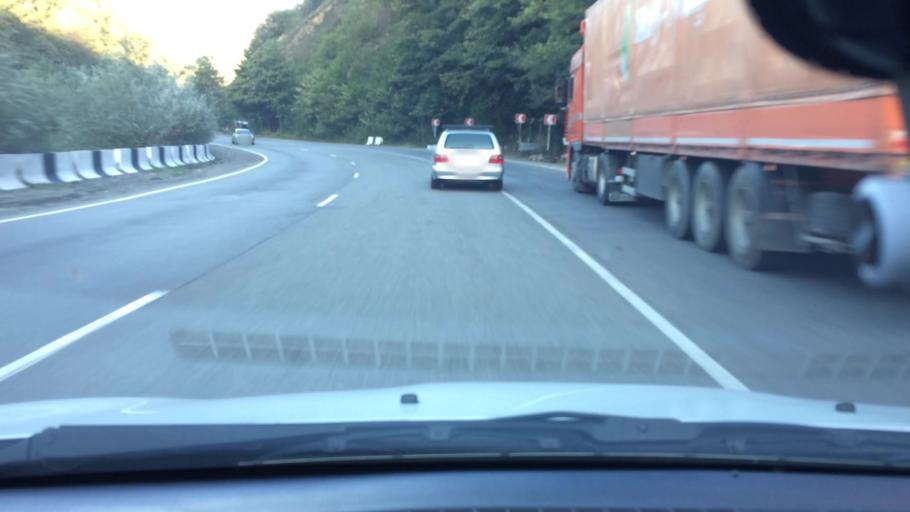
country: GE
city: Surami
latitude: 42.0941
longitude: 43.4596
